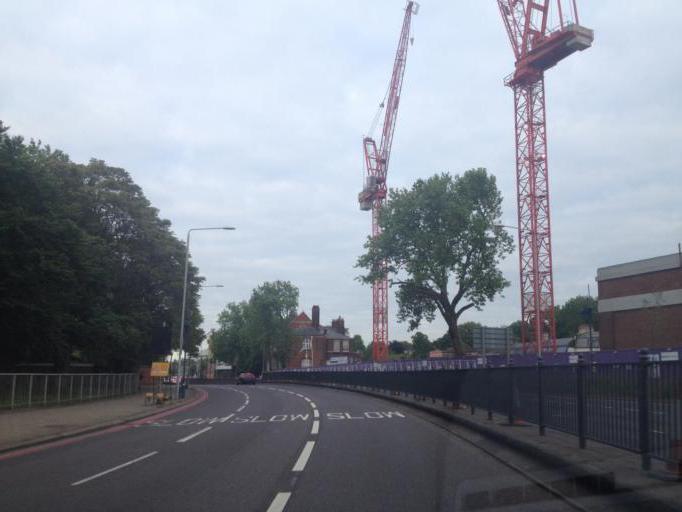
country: GB
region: England
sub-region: Greater London
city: Hammersmith
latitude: 51.4909
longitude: -0.2174
